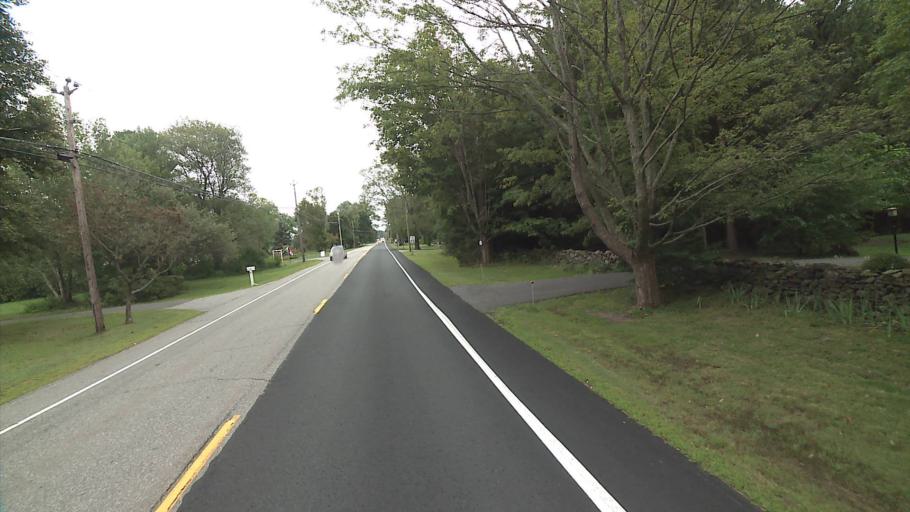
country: US
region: Connecticut
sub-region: Hartford County
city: Manchester
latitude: 41.7484
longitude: -72.4381
